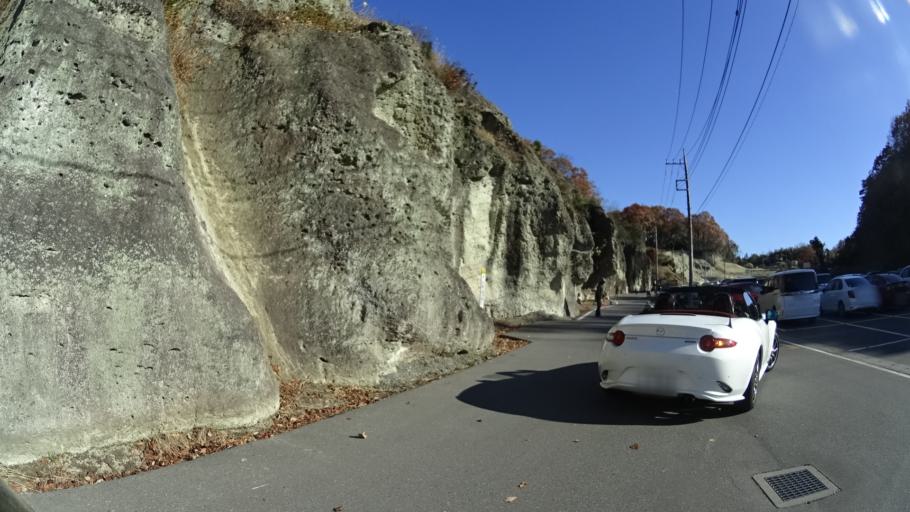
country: JP
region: Tochigi
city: Utsunomiya-shi
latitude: 36.5992
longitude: 139.8220
